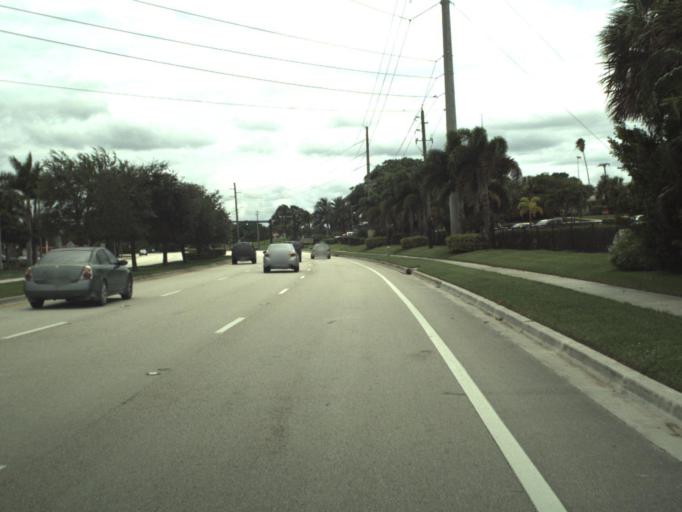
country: US
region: Florida
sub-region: Palm Beach County
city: North Palm Beach
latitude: 26.8280
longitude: -80.0611
